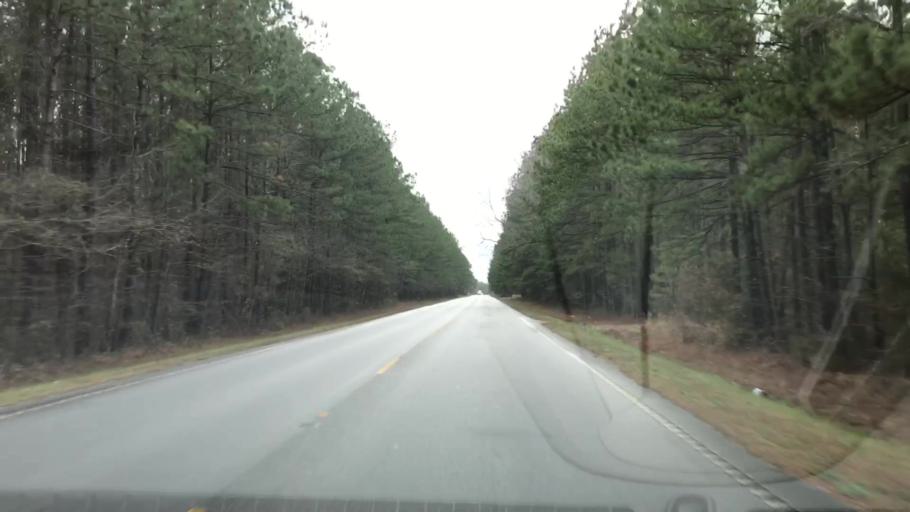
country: US
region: South Carolina
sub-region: Williamsburg County
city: Andrews
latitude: 33.2838
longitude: -79.7166
